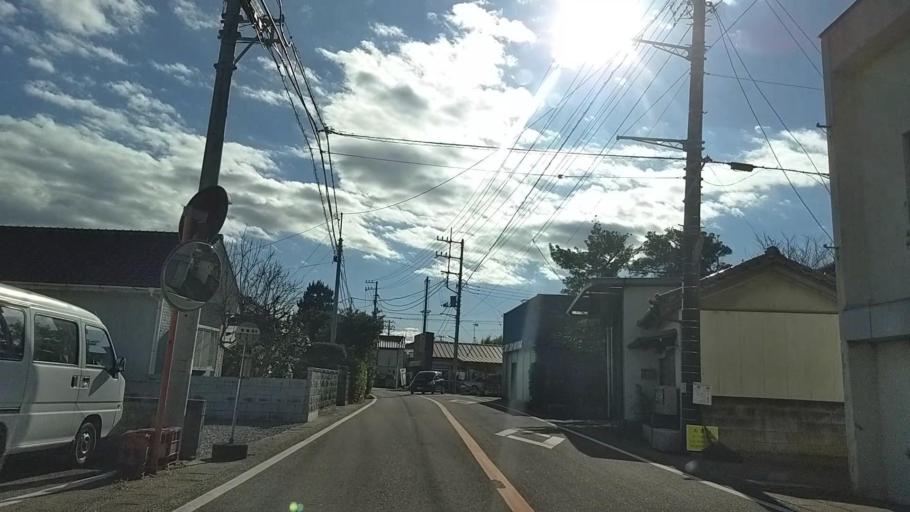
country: JP
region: Chiba
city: Tateyama
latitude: 35.0288
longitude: 139.8424
